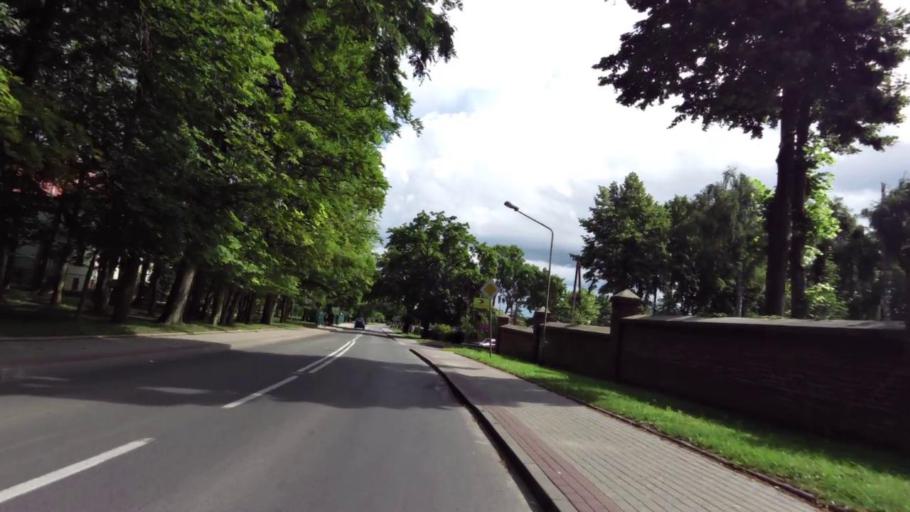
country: PL
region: West Pomeranian Voivodeship
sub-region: Powiat slawienski
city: Darlowo
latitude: 54.4254
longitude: 16.4160
